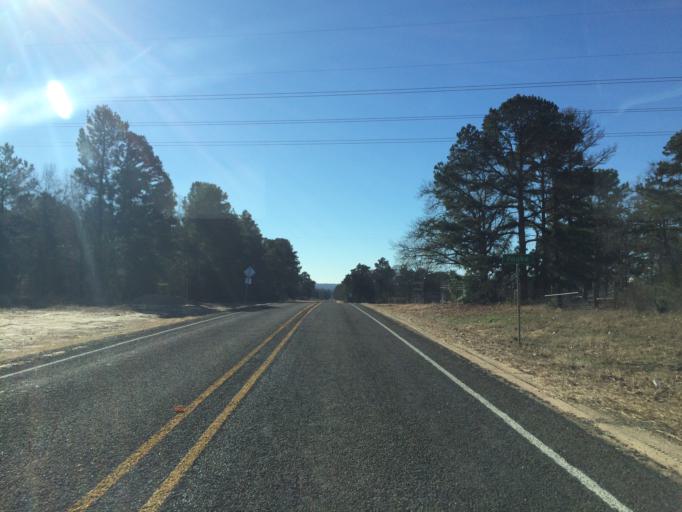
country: US
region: Texas
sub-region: Wood County
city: Hawkins
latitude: 32.6304
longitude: -95.2743
